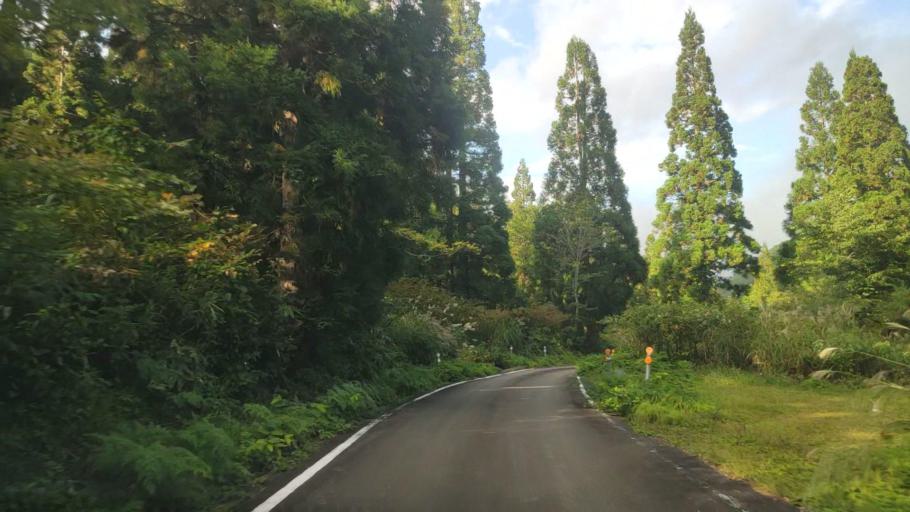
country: JP
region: Toyama
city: Yatsuomachi-higashikumisaka
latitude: 36.3685
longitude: 137.0759
